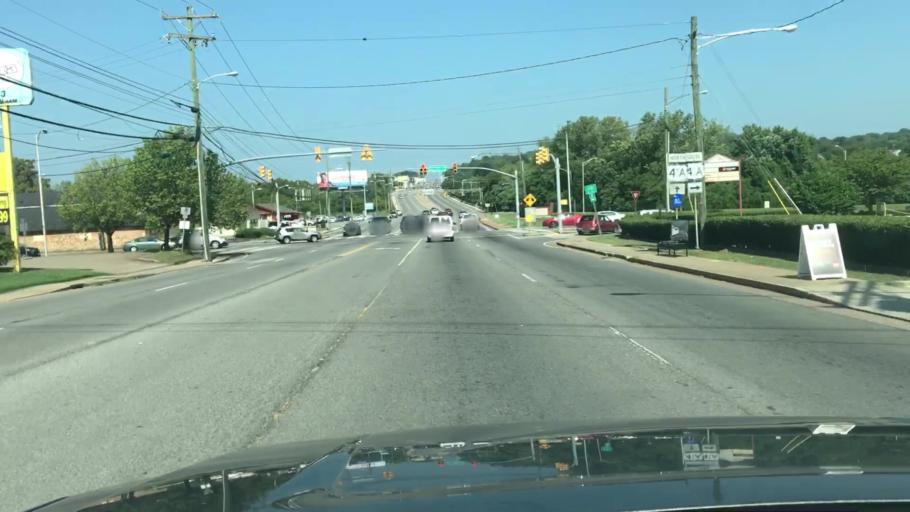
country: US
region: Tennessee
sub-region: Davidson County
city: Nashville
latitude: 36.1876
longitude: -86.8208
